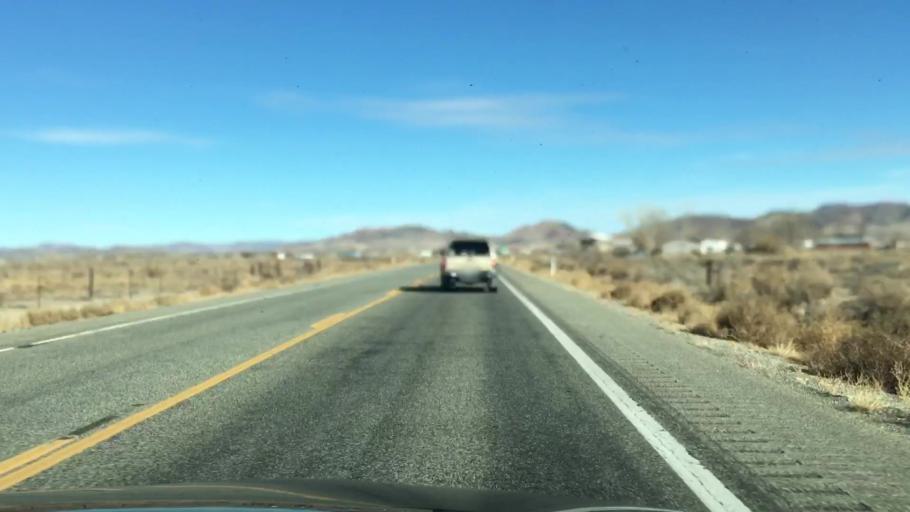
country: US
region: Nevada
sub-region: Lyon County
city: Yerington
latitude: 39.0040
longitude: -119.0902
